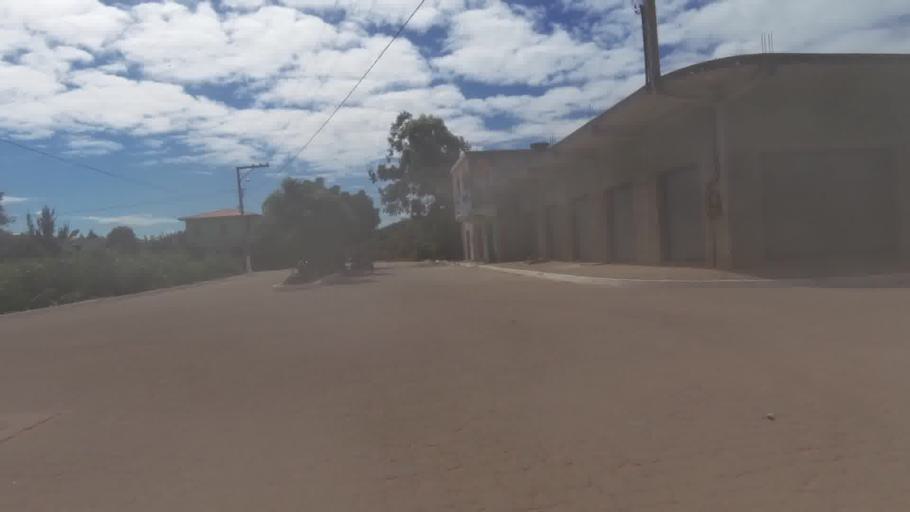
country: BR
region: Espirito Santo
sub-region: Marataizes
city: Marataizes
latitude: -21.1898
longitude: -40.9296
